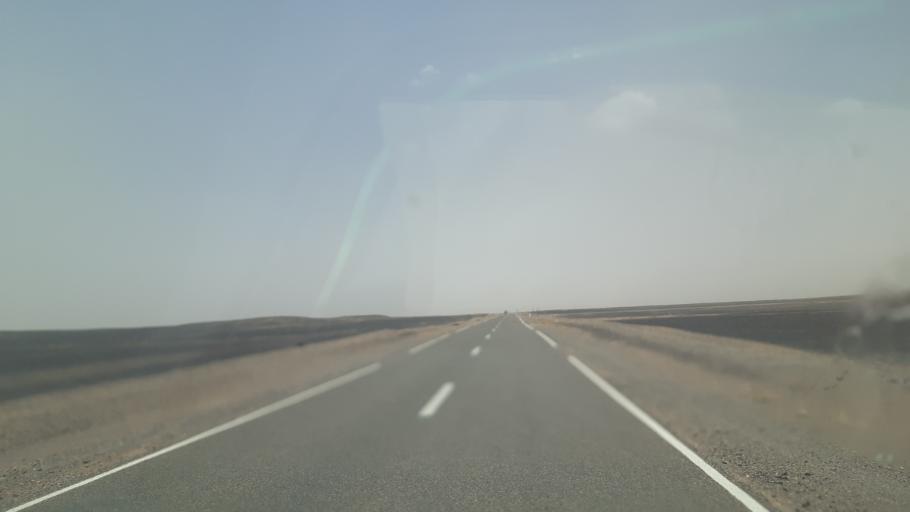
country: MA
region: Meknes-Tafilalet
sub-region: Errachidia
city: Jorf
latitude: 31.1551
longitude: -4.0643
